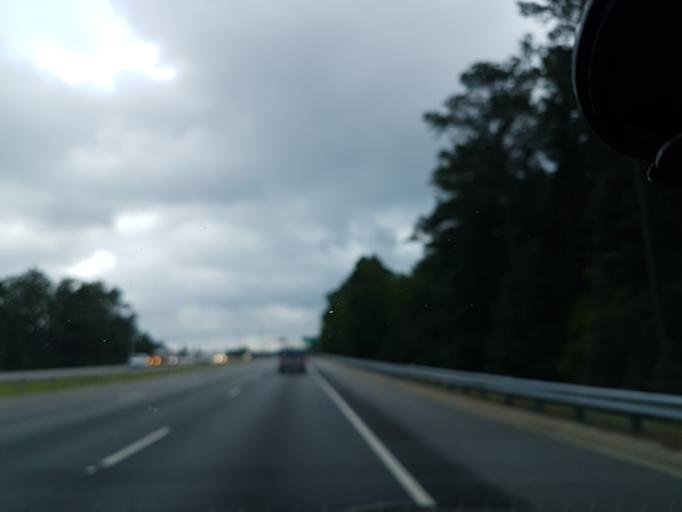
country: US
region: Georgia
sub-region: DeKalb County
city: Tucker
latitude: 33.8347
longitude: -84.2064
